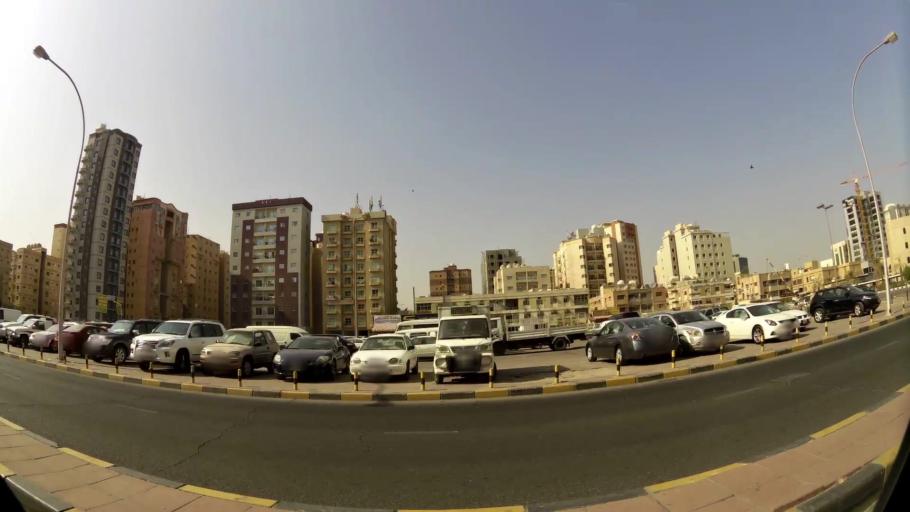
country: KW
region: Muhafazat Hawalli
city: Hawalli
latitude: 29.3308
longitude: 48.0105
